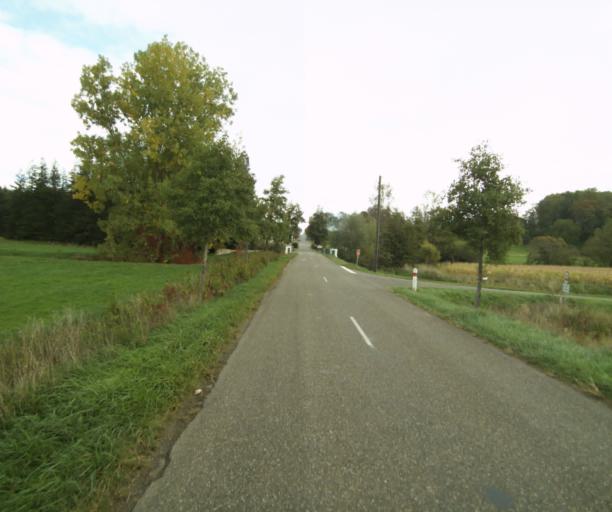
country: FR
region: Midi-Pyrenees
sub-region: Departement du Gers
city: Cazaubon
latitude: 43.8633
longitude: -0.0065
